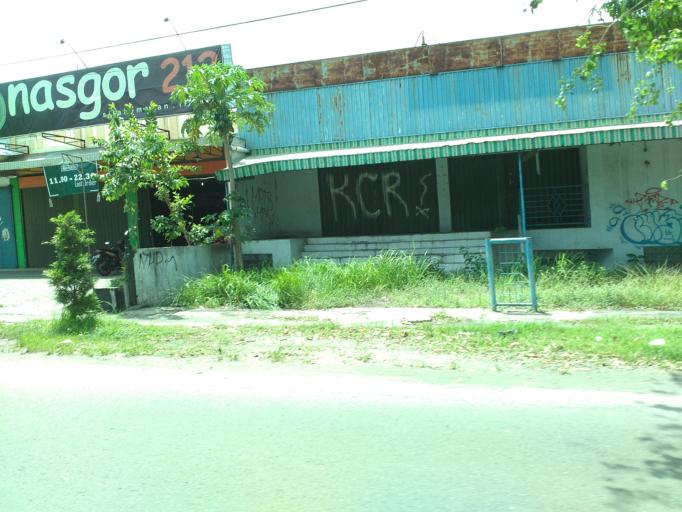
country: ID
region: Central Java
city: Klaten
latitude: -7.6896
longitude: 110.6064
